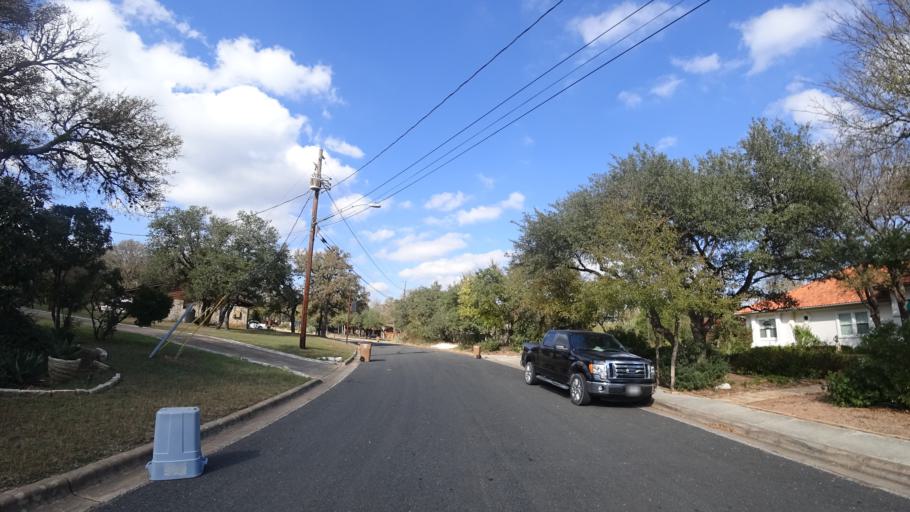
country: US
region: Texas
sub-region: Travis County
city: Shady Hollow
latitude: 30.1798
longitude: -97.8497
